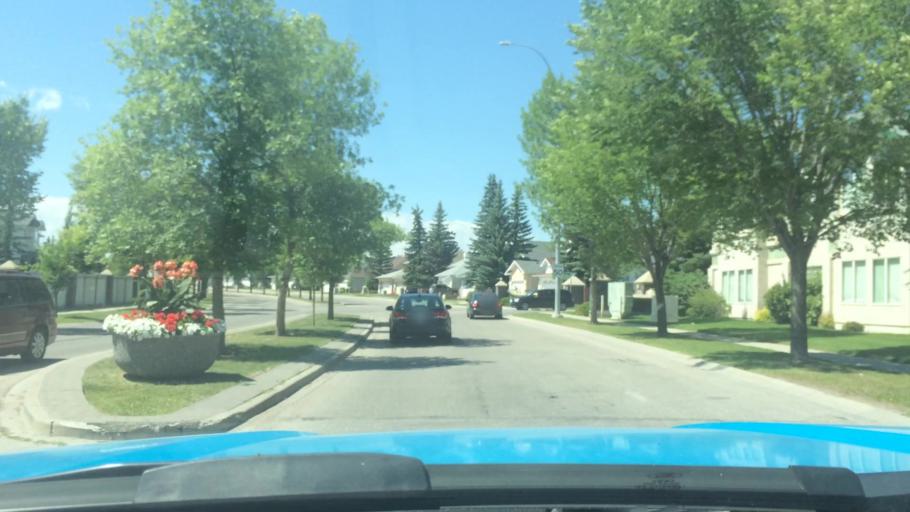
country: CA
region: Alberta
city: Calgary
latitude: 51.1378
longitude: -114.1858
